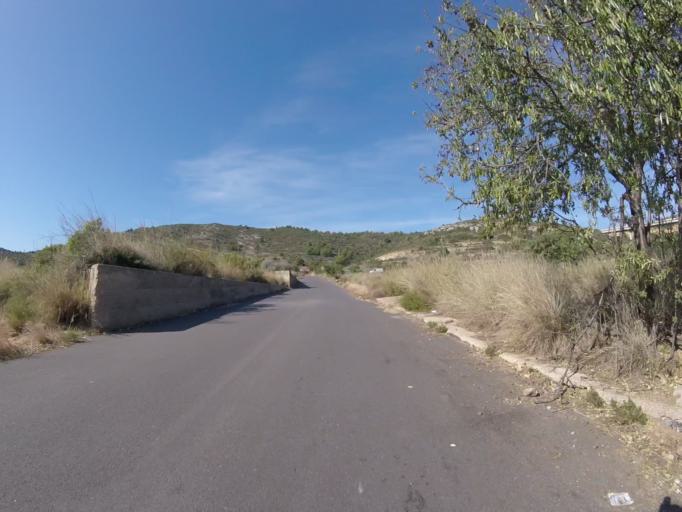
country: ES
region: Valencia
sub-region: Provincia de Castello
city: Torreblanca
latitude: 40.2239
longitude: 0.1850
